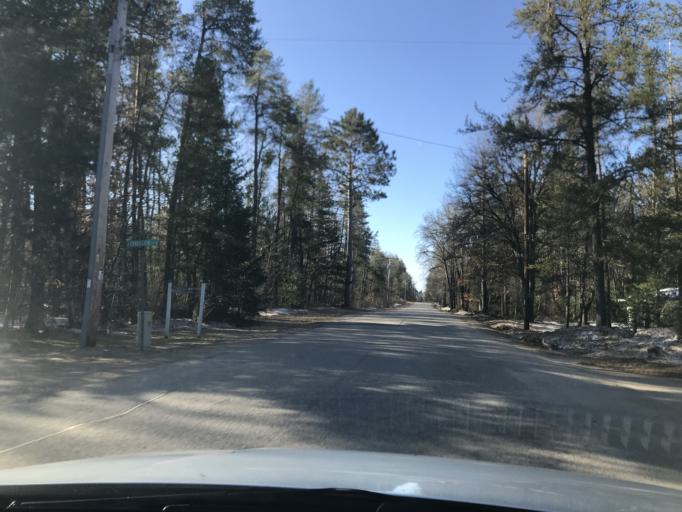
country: US
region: Michigan
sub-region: Dickinson County
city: Kingsford
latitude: 45.3935
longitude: -88.1612
